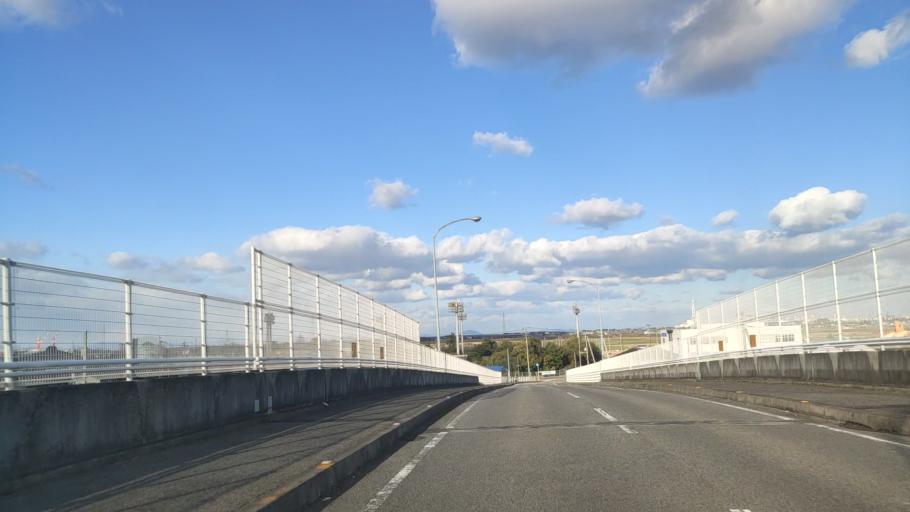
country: JP
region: Ehime
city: Saijo
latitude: 33.8966
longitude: 133.1330
